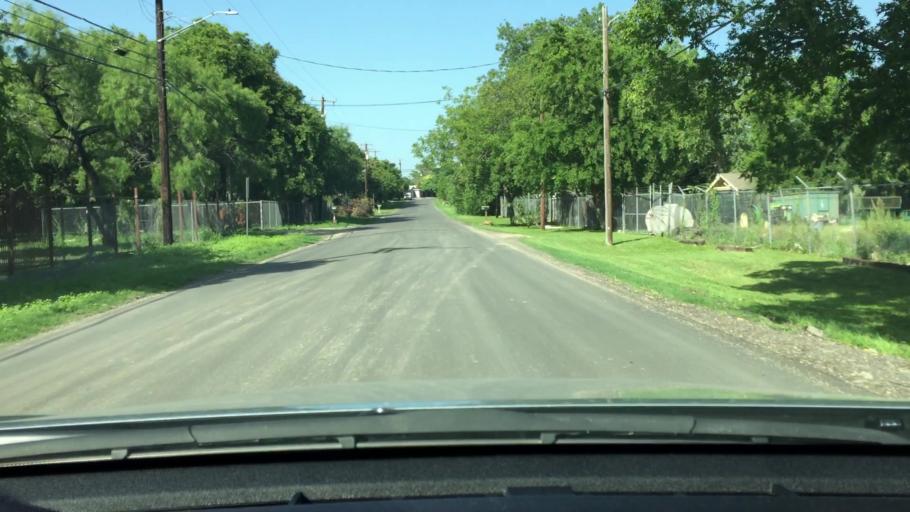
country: US
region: Texas
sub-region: Bexar County
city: Windcrest
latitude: 29.5292
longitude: -98.3863
